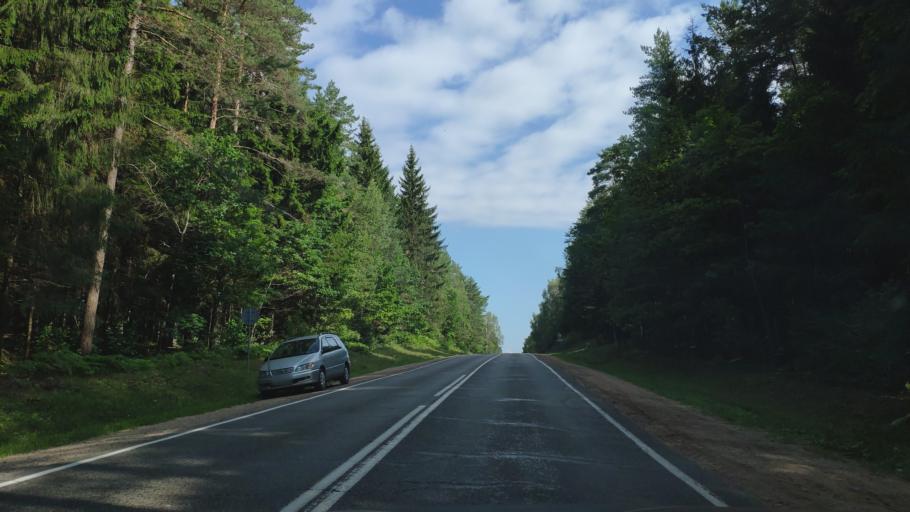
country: BY
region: Minsk
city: Novosel'ye
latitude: 53.9419
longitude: 27.2447
